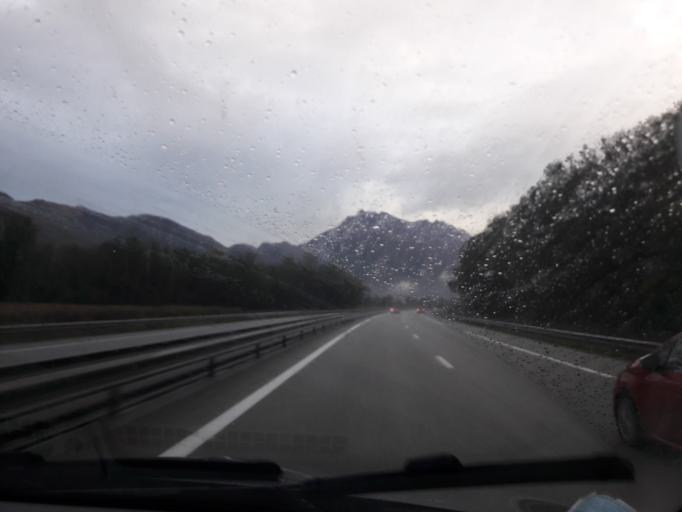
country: FR
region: Rhone-Alpes
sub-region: Departement de la Savoie
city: Cruet
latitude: 45.5222
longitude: 6.1139
